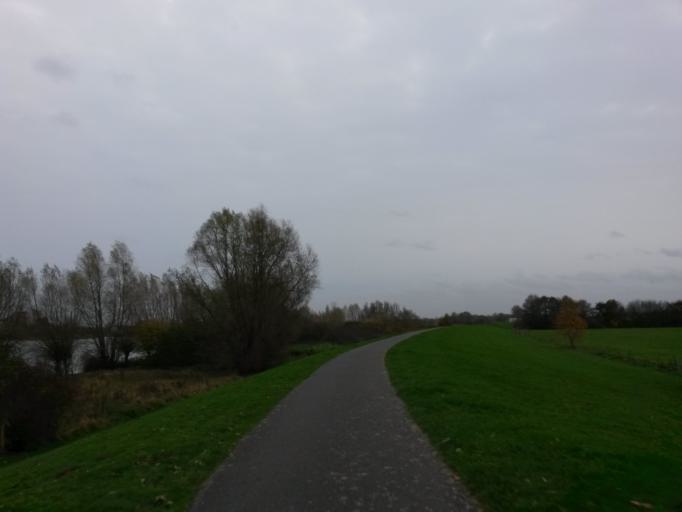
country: DE
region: Bremen
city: Bremen
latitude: 53.0519
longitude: 8.8717
